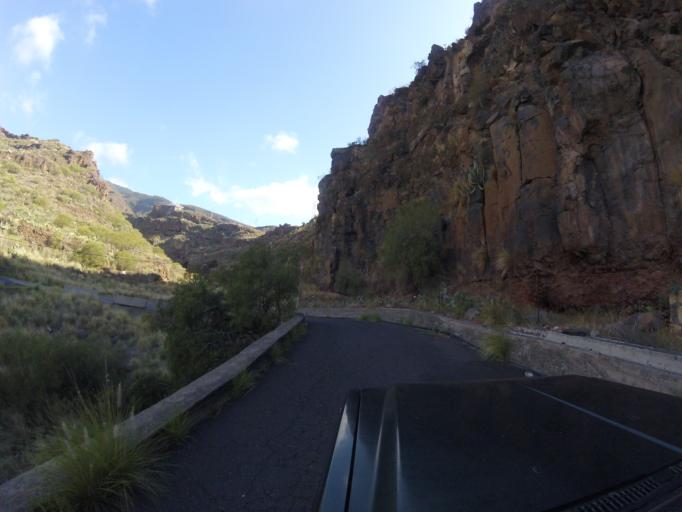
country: ES
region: Canary Islands
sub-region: Provincia de Santa Cruz de Tenerife
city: Candelaria
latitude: 28.3790
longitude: -16.3744
